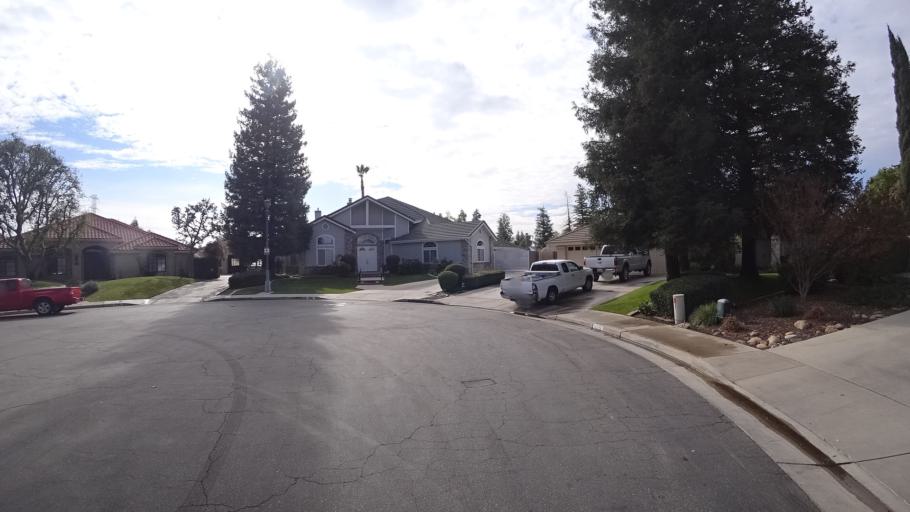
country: US
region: California
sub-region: Kern County
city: Greenacres
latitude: 35.3998
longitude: -119.0789
